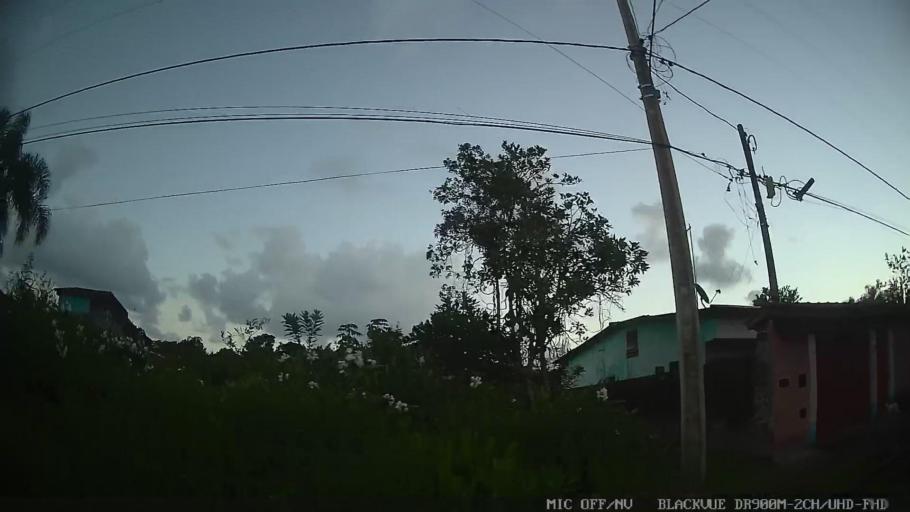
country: BR
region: Sao Paulo
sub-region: Itanhaem
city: Itanhaem
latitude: -24.1450
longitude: -46.7424
